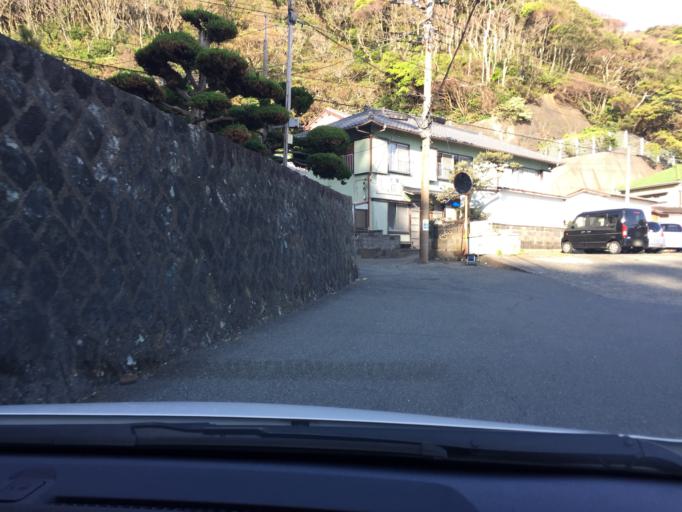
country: JP
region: Shizuoka
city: Shimoda
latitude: 34.6564
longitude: 138.9697
